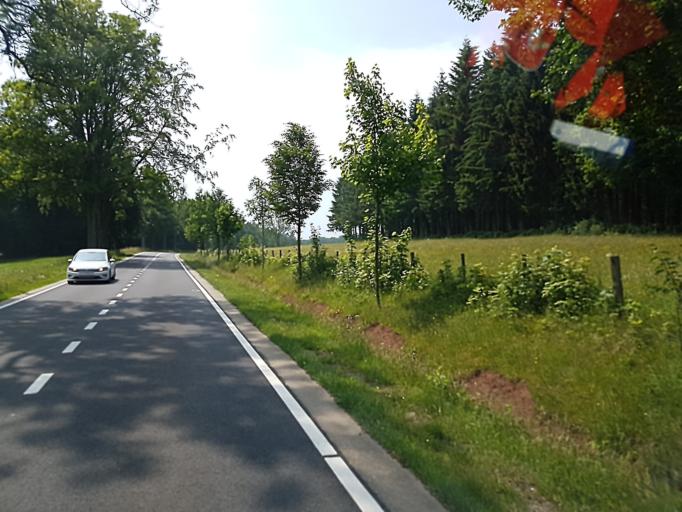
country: BE
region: Wallonia
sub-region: Province de Liege
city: Stoumont
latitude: 50.3470
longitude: 5.8149
